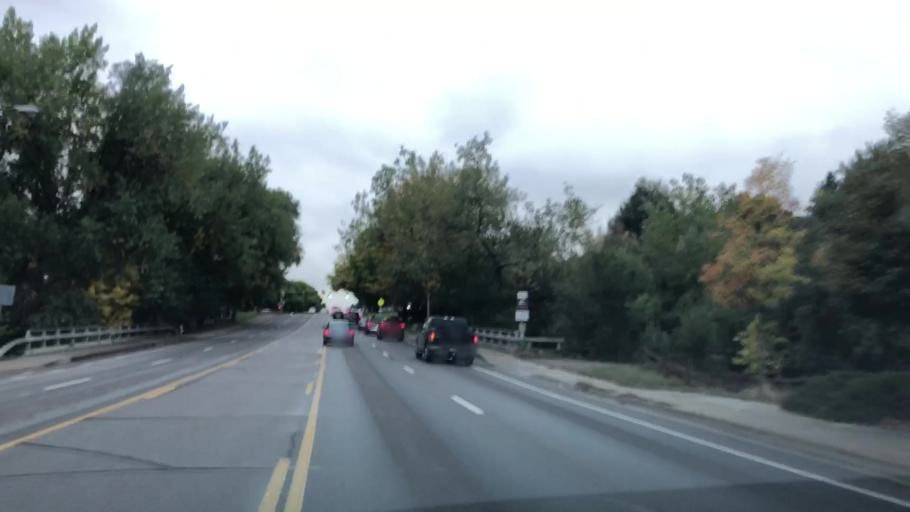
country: US
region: Colorado
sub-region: Larimer County
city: Fort Collins
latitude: 40.5657
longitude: -105.0580
